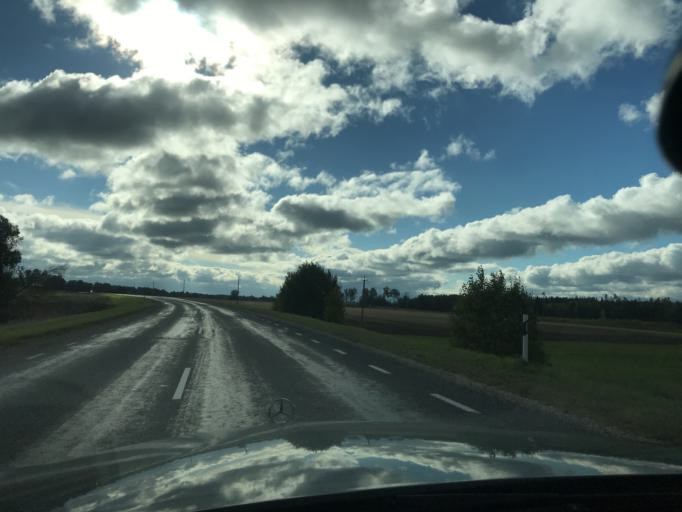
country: EE
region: Valgamaa
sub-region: Valga linn
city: Valga
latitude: 57.9720
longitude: 26.2607
